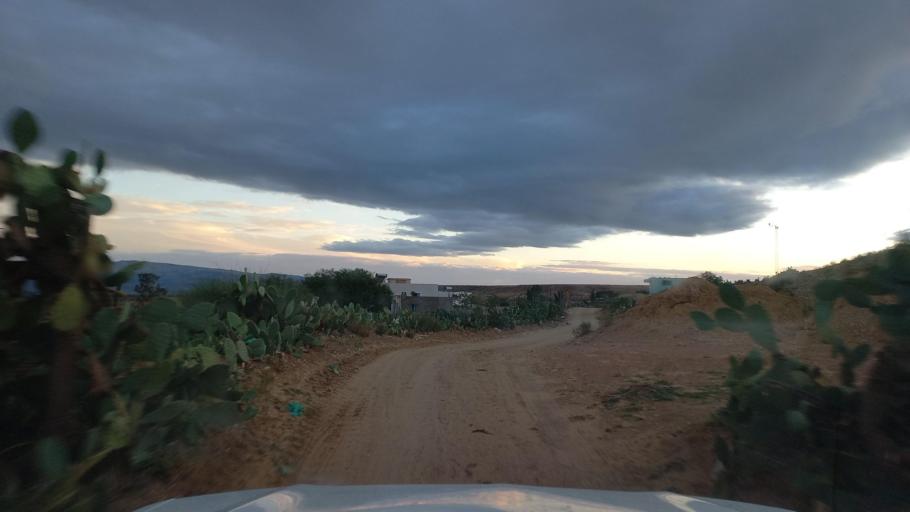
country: TN
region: Al Qasrayn
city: Kasserine
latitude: 35.2576
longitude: 8.9358
